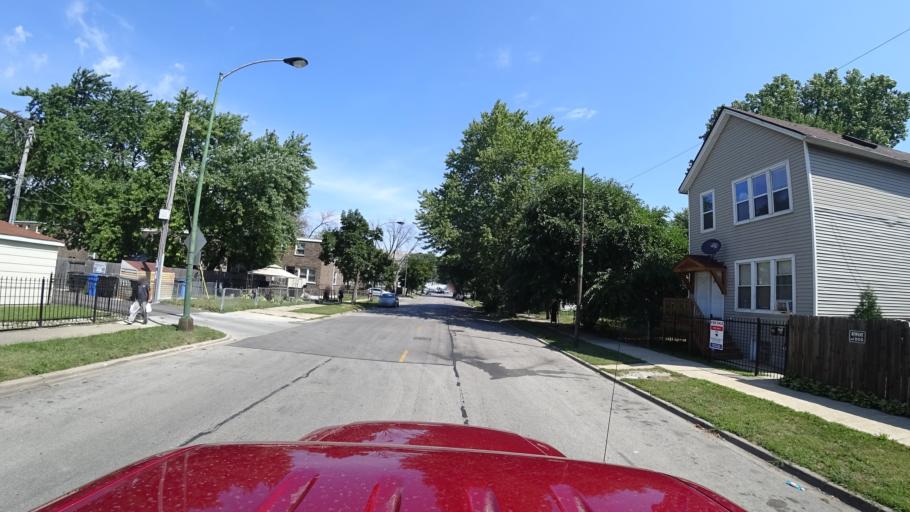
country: US
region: Illinois
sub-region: Cook County
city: Chicago
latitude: 41.8176
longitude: -87.6336
